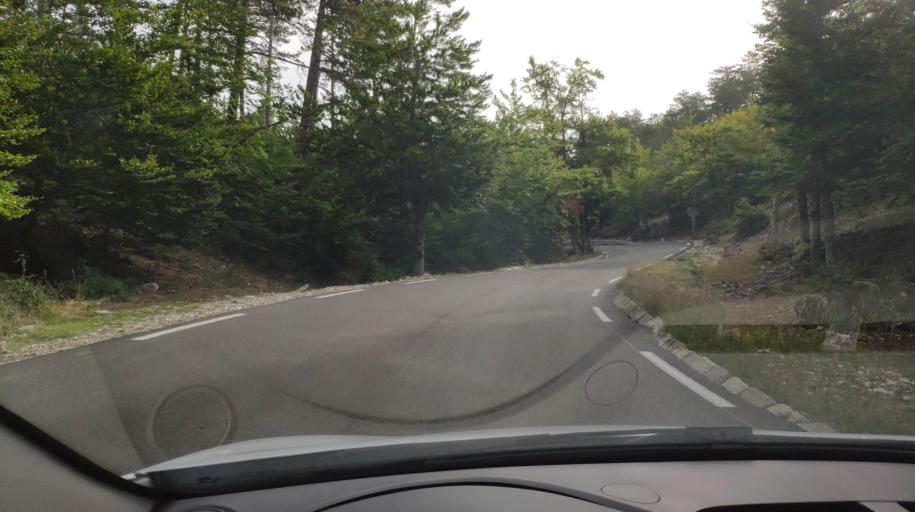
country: FR
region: Provence-Alpes-Cote d'Azur
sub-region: Departement du Vaucluse
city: Sault
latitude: 44.1384
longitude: 5.3106
